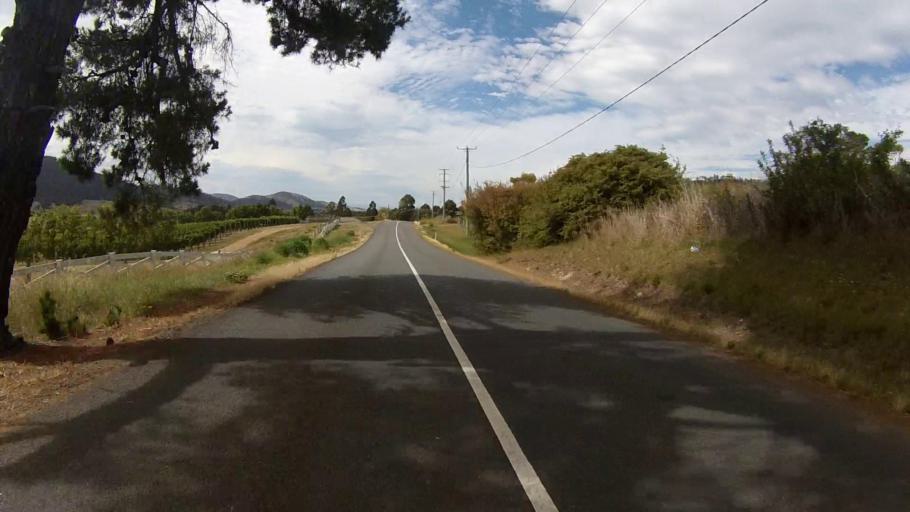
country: AU
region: Tasmania
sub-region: Brighton
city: Old Beach
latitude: -42.7069
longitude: 147.3685
